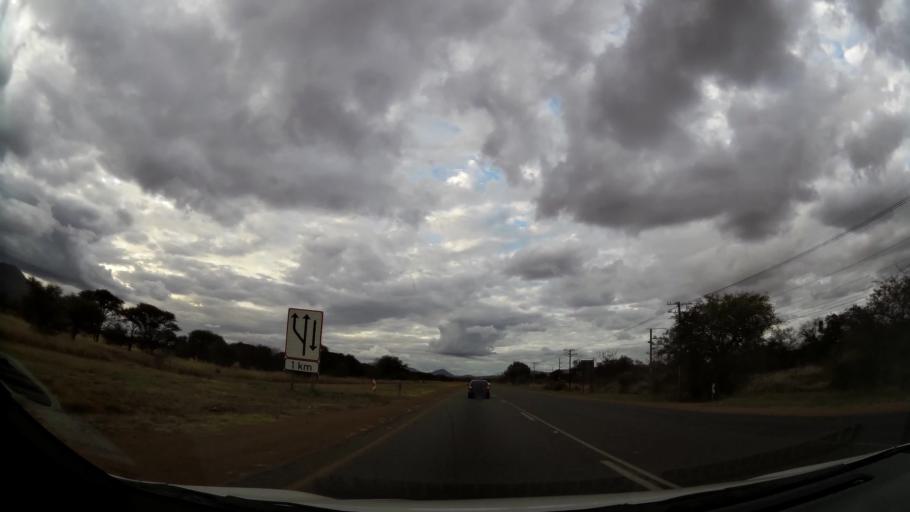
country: ZA
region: Limpopo
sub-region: Waterberg District Municipality
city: Mokopane
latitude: -24.2479
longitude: 28.9915
